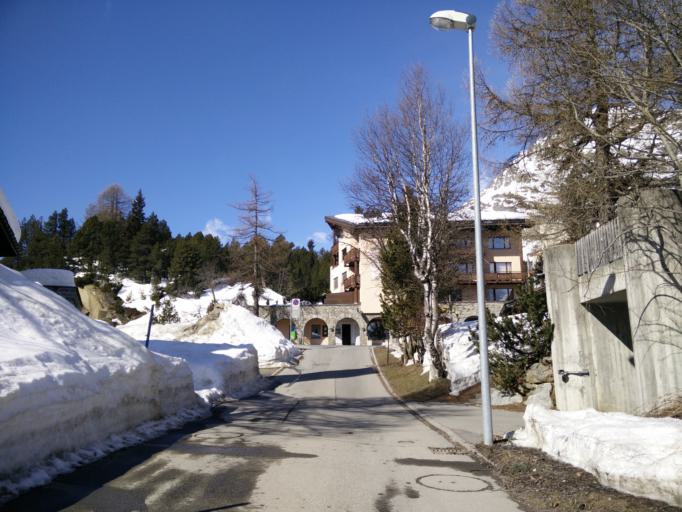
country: CH
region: Grisons
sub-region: Maloja District
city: Silvaplana
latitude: 46.4025
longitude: 9.6962
